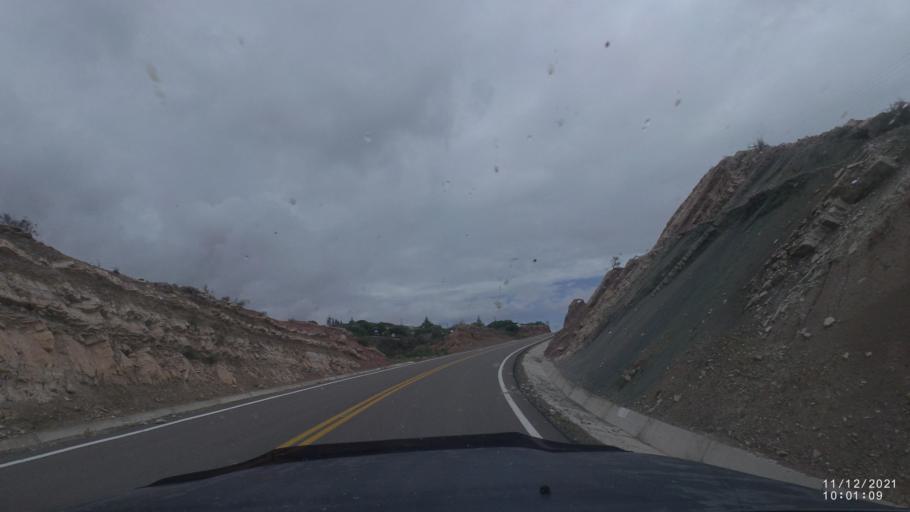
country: BO
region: Cochabamba
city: Cliza
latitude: -17.7312
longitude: -65.9275
